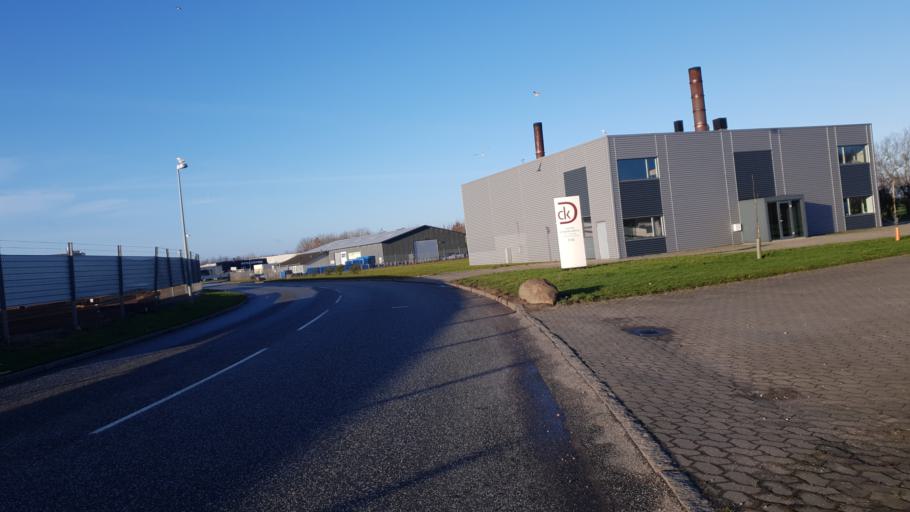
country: DK
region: Central Jutland
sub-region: Hedensted Kommune
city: Hedensted
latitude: 55.7968
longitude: 9.6782
